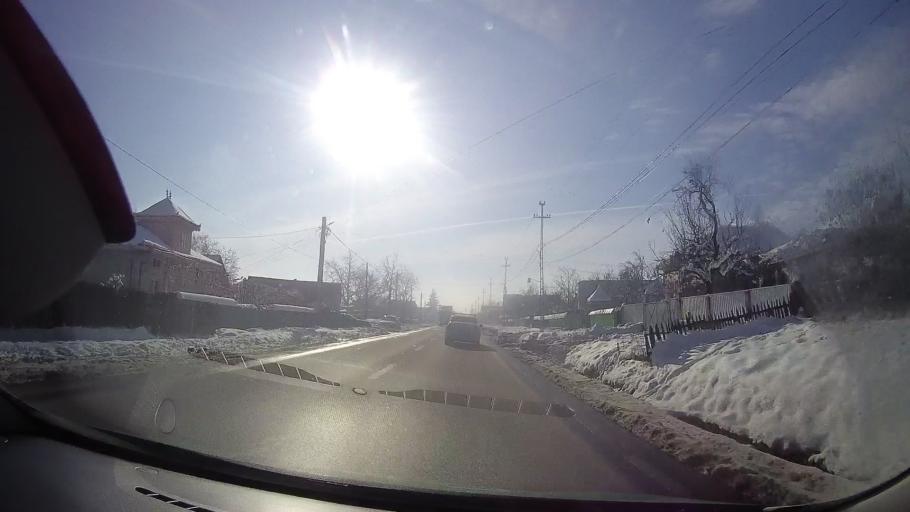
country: RO
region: Iasi
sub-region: Comuna Motca
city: Motca
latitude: 47.2507
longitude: 26.6091
